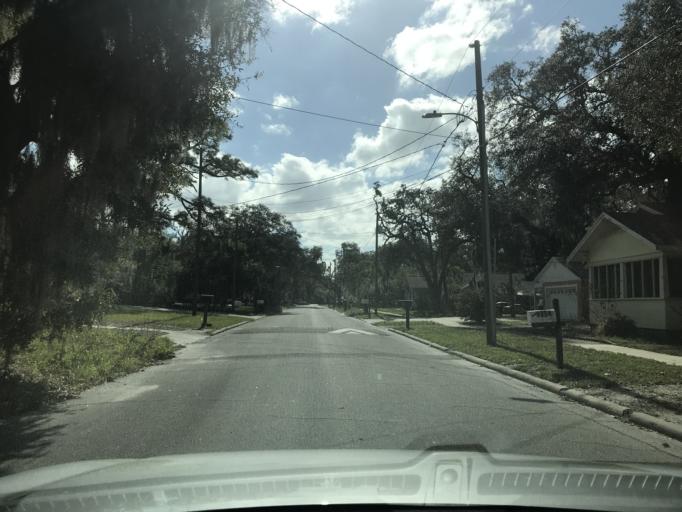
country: US
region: Florida
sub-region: Pinellas County
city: Belleair
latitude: 27.9478
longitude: -82.7892
